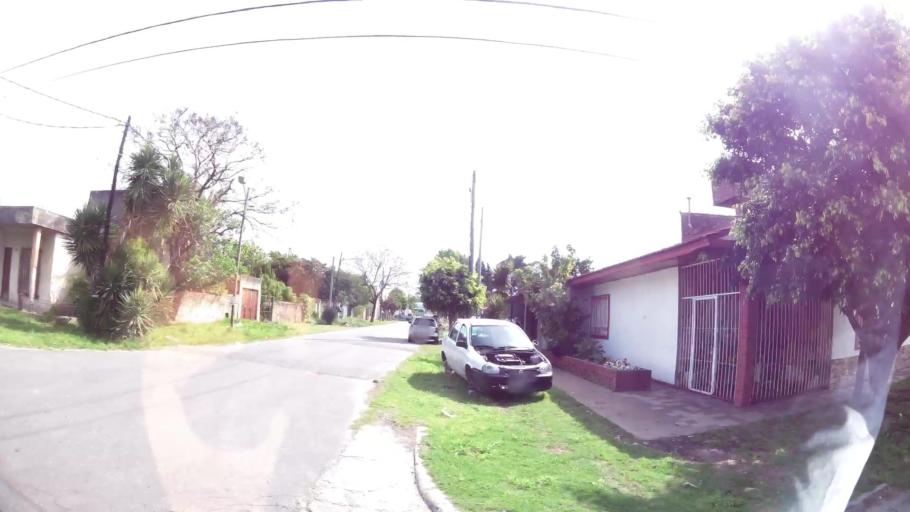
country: AR
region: Buenos Aires
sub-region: Partido de Quilmes
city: Quilmes
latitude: -34.7738
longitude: -58.2382
